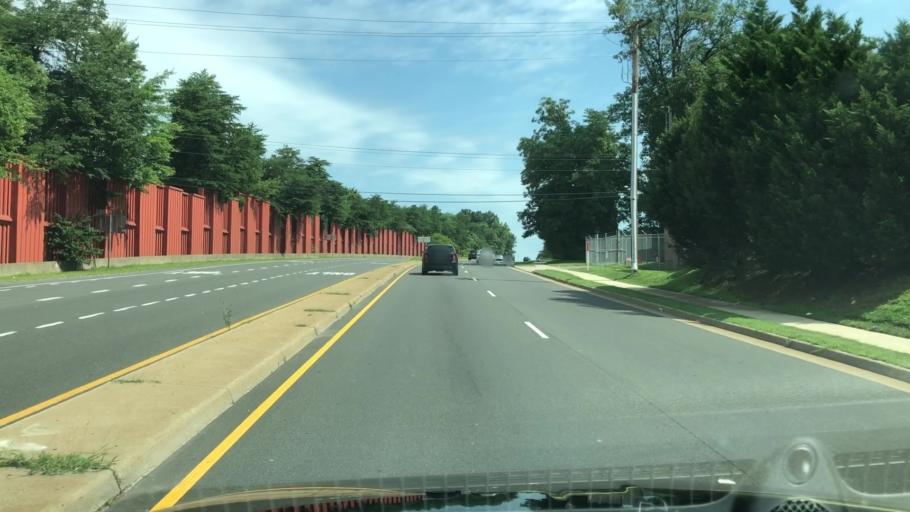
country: US
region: Virginia
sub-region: Prince William County
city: Dale City
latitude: 38.6286
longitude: -77.3030
